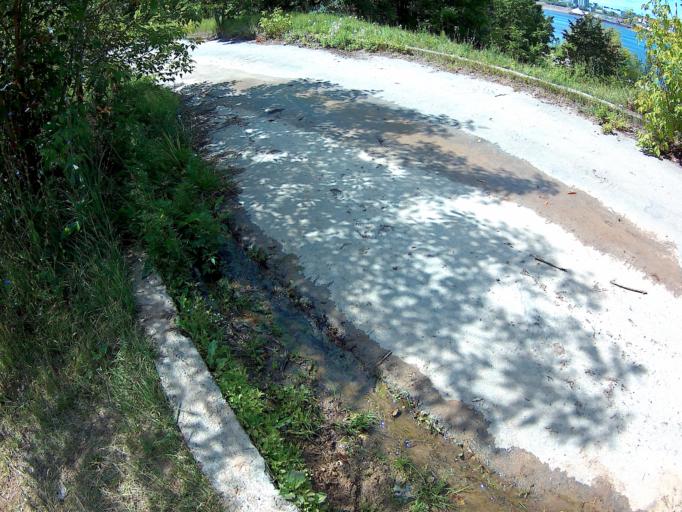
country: RU
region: Nizjnij Novgorod
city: Nizhniy Novgorod
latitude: 56.2369
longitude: 43.9356
